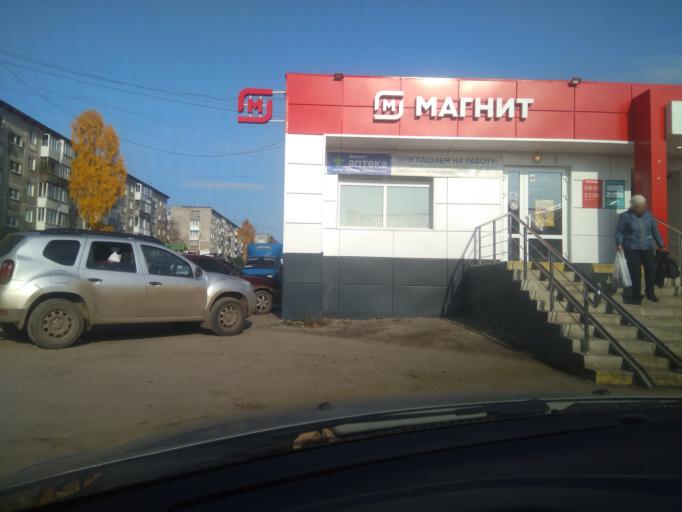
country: RU
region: Sverdlovsk
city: Nizhniye Sergi
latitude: 56.6631
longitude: 59.3032
